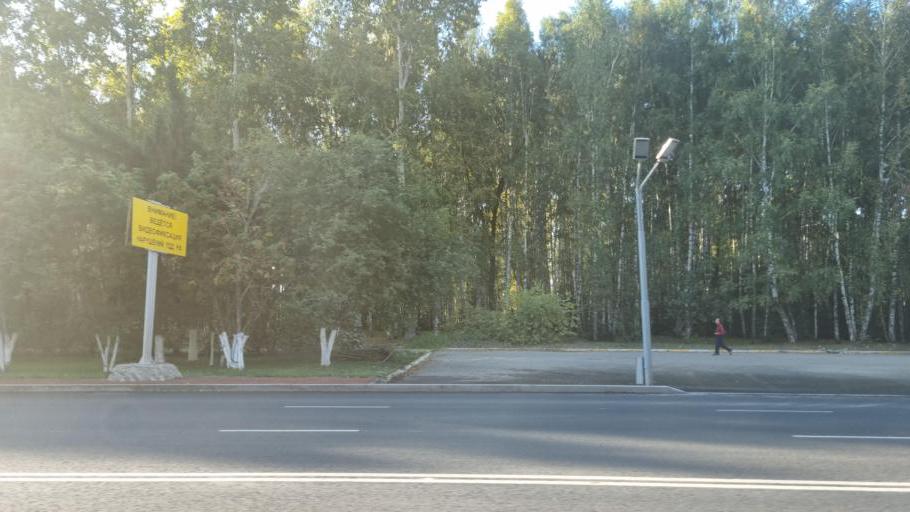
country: RU
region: Tomsk
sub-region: Tomskiy Rayon
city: Tomsk
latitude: 56.4552
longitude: 84.9550
